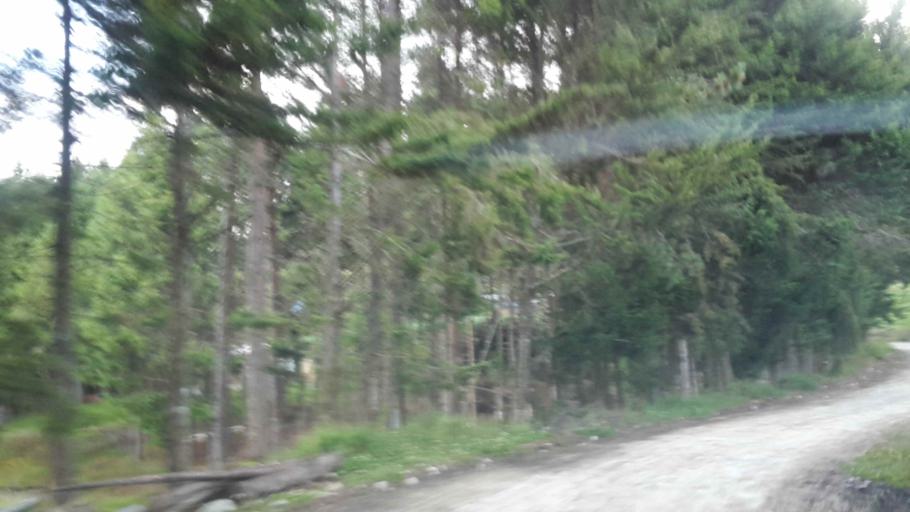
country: BO
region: Cochabamba
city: Colomi
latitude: -17.2549
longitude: -65.9040
